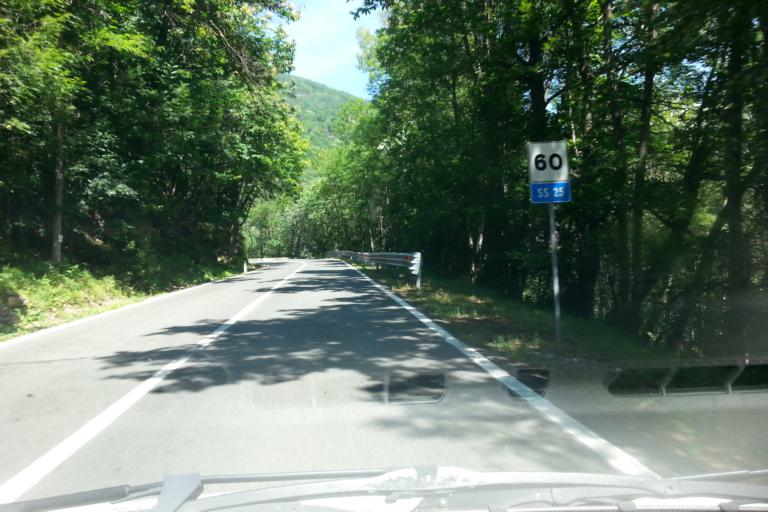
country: IT
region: Piedmont
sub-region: Provincia di Torino
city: Venaus
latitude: 45.1513
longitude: 6.9986
